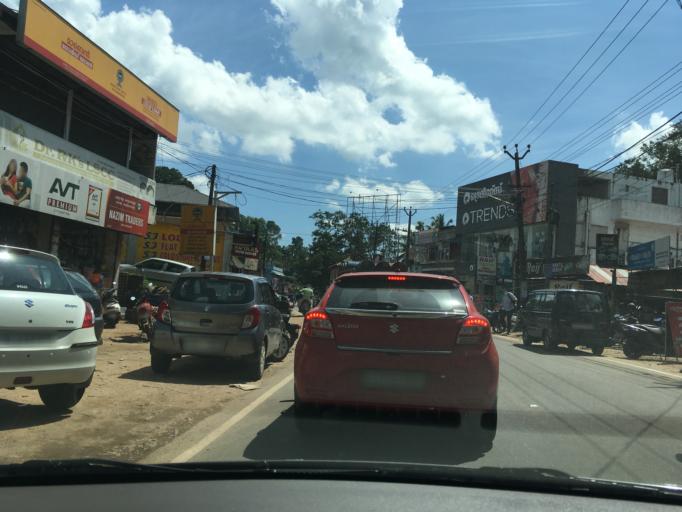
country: IN
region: Kerala
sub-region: Thiruvananthapuram
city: Nedumangad
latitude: 8.6018
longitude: 76.9960
